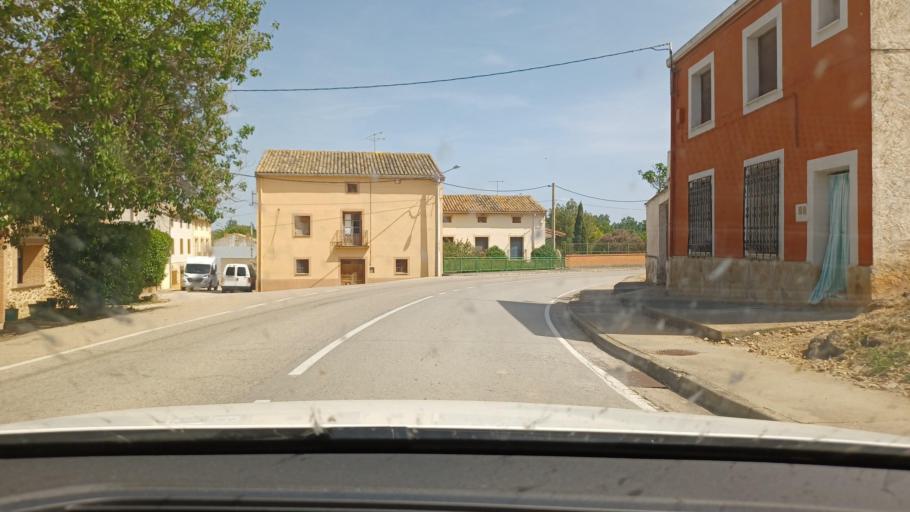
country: ES
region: Castille and Leon
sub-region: Provincia de Soria
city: Monteagudo de las Vicarias
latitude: 41.3645
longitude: -2.1684
